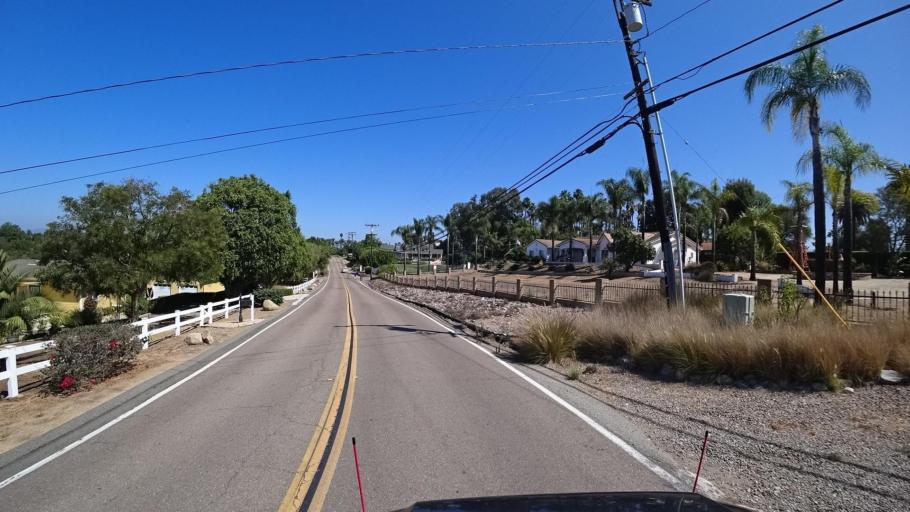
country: US
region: California
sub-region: San Diego County
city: Fallbrook
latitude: 33.3401
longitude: -117.2153
